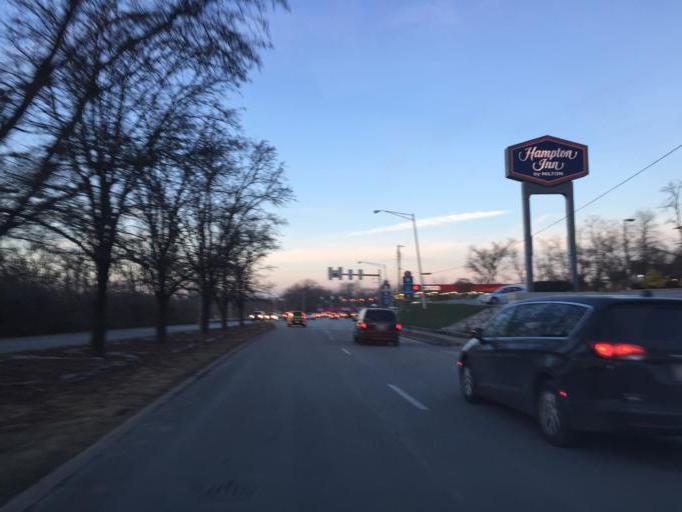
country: US
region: Indiana
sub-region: Monroe County
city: Bloomington
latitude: 39.1844
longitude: -86.5344
